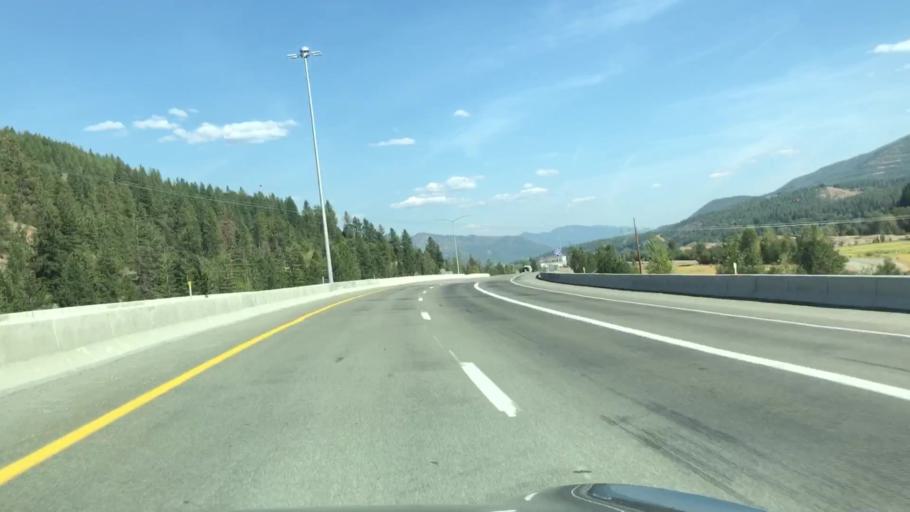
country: US
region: Idaho
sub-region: Shoshone County
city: Pinehurst
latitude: 47.5479
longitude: -116.2217
